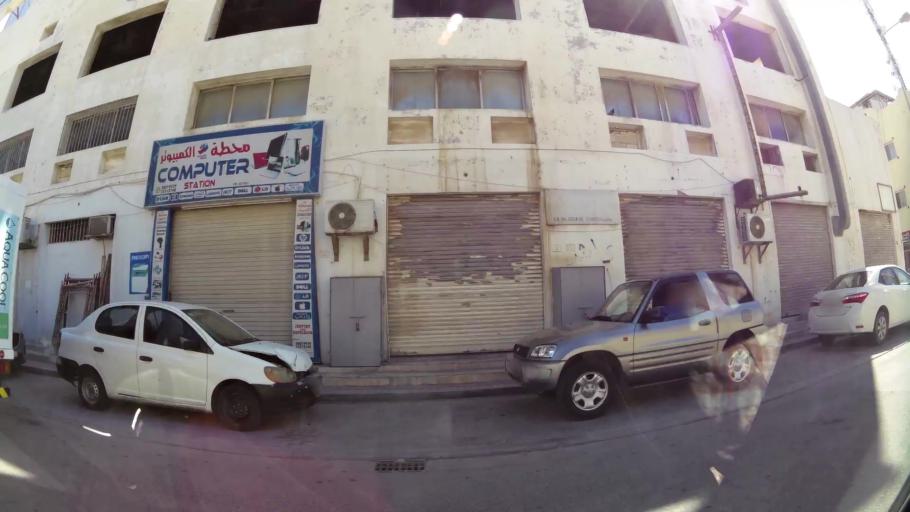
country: BH
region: Muharraq
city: Al Muharraq
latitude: 26.2441
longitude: 50.6129
